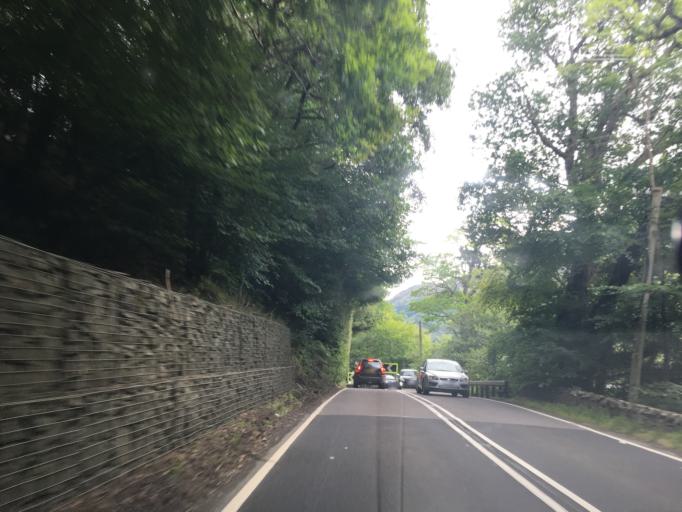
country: GB
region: Scotland
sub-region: Stirling
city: Callander
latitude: 56.3032
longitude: -4.3174
